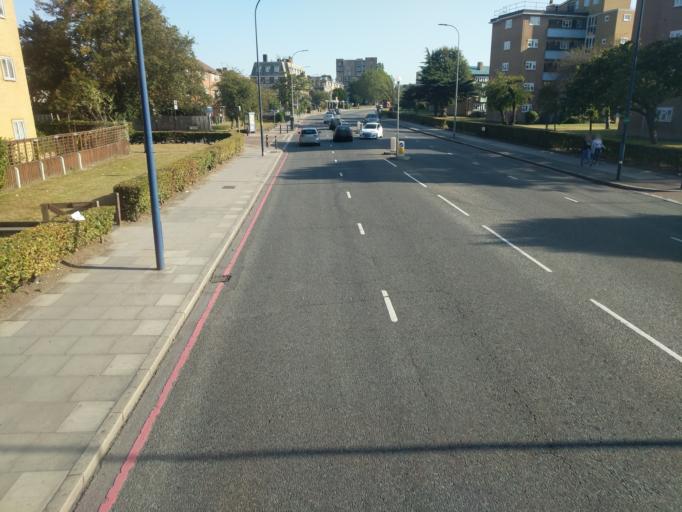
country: GB
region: England
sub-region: Greater London
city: Catford
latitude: 51.4320
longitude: -0.0166
